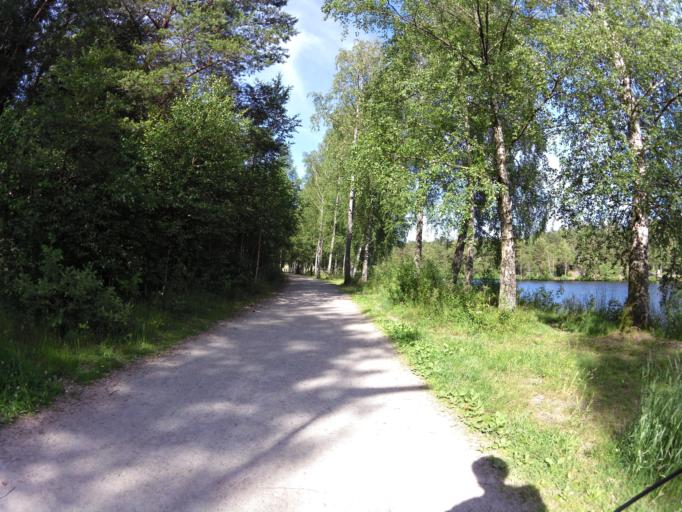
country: NO
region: Ostfold
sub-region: Fredrikstad
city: Fredrikstad
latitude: 59.2304
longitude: 10.9450
